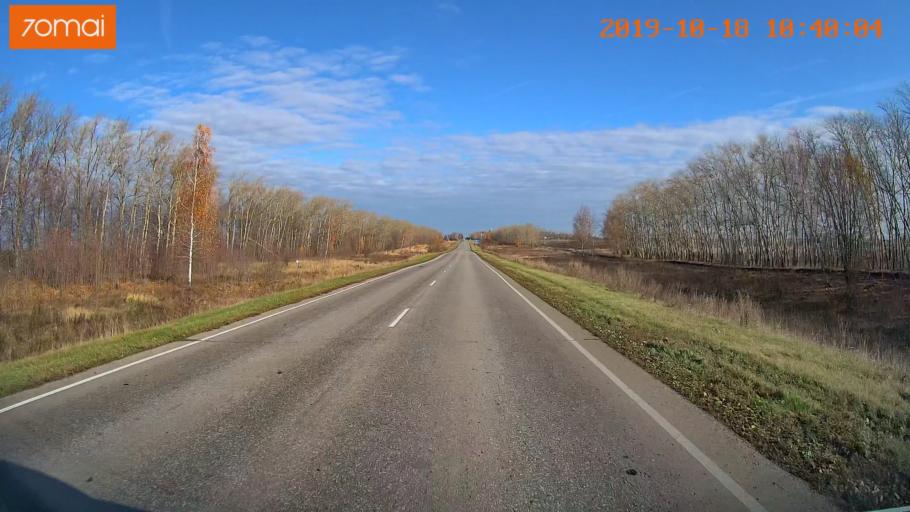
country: RU
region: Tula
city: Kurkino
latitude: 53.5958
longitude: 38.6599
